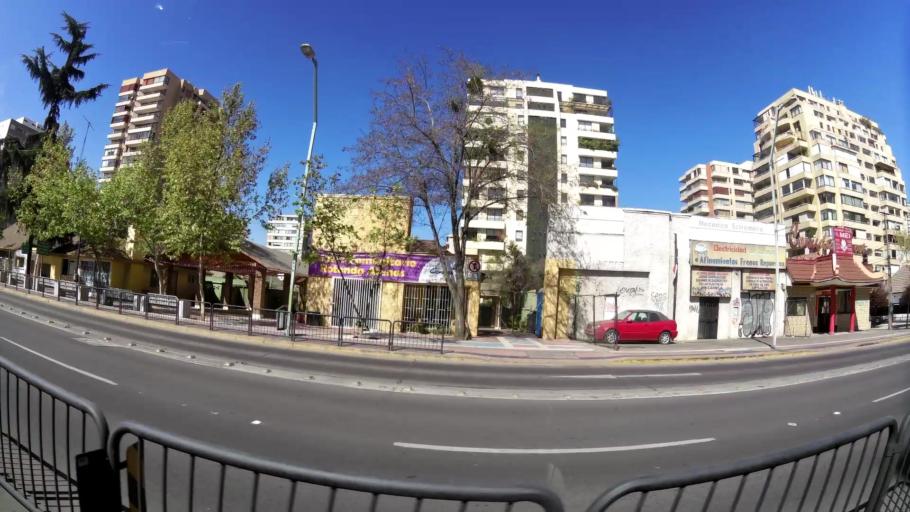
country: CL
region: Santiago Metropolitan
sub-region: Provincia de Santiago
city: Villa Presidente Frei, Nunoa, Santiago, Chile
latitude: -33.4181
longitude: -70.5552
